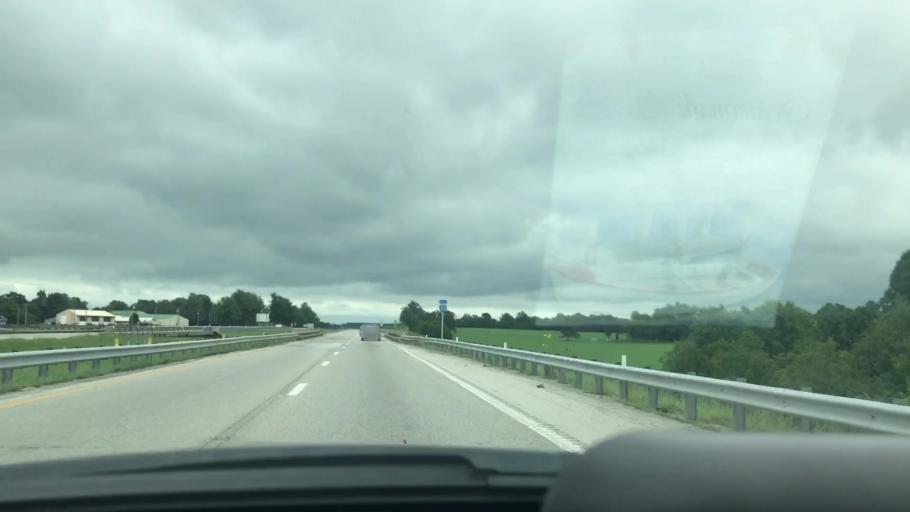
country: US
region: Missouri
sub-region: Lawrence County
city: Mount Vernon
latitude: 37.0964
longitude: -93.7977
